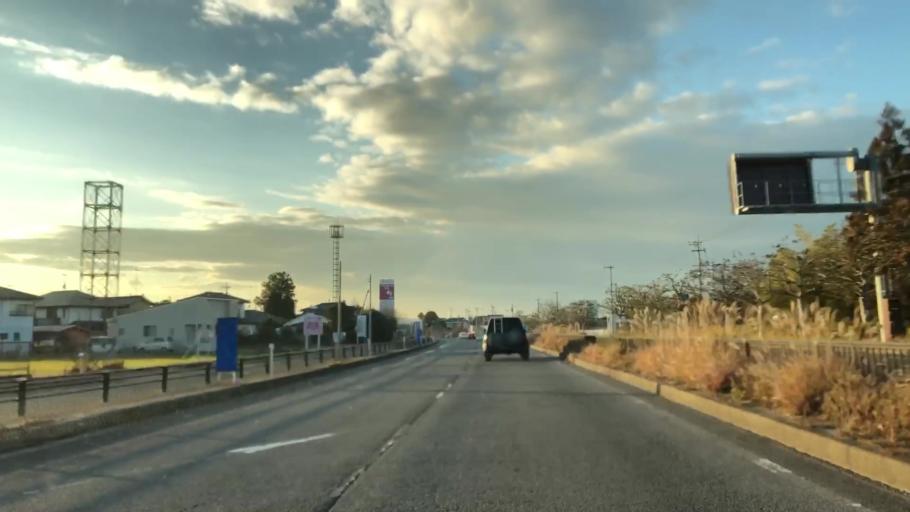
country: JP
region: Fukuoka
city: Nakatsu
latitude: 33.5596
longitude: 131.1979
